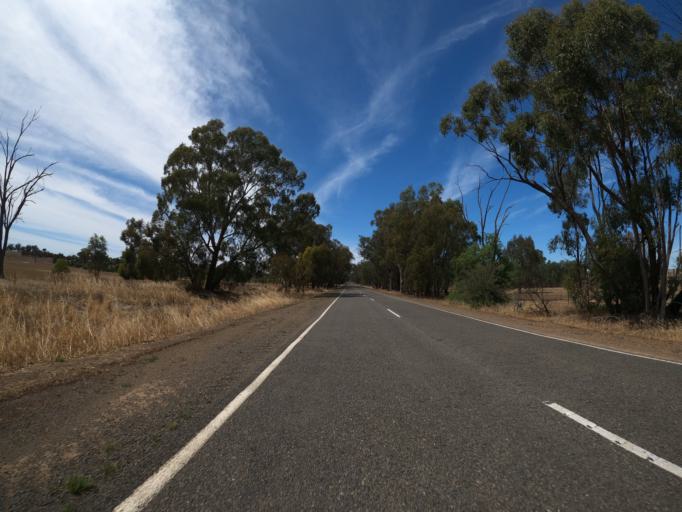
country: AU
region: Victoria
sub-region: Benalla
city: Benalla
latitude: -36.3547
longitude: 145.9647
